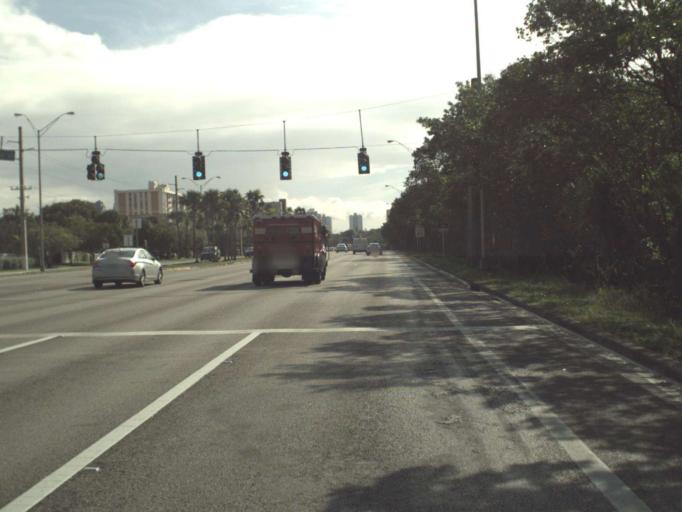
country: US
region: Florida
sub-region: Miami-Dade County
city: North Miami Beach
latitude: 25.9259
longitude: -80.1477
